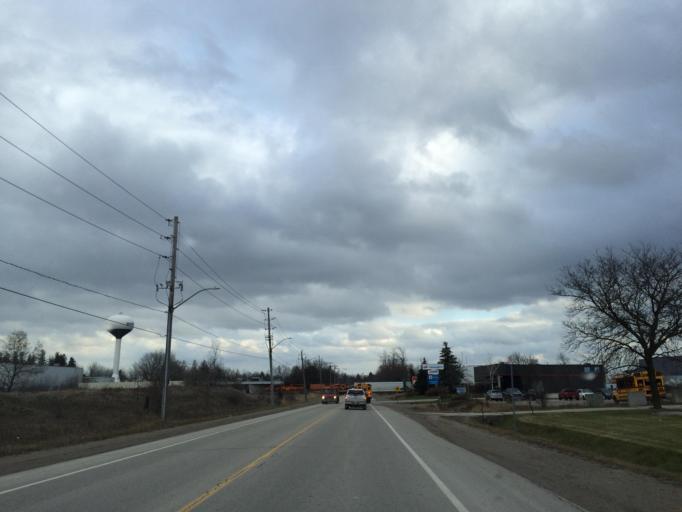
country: CA
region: Ontario
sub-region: Wellington County
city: Guelph
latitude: 43.5405
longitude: -80.3017
